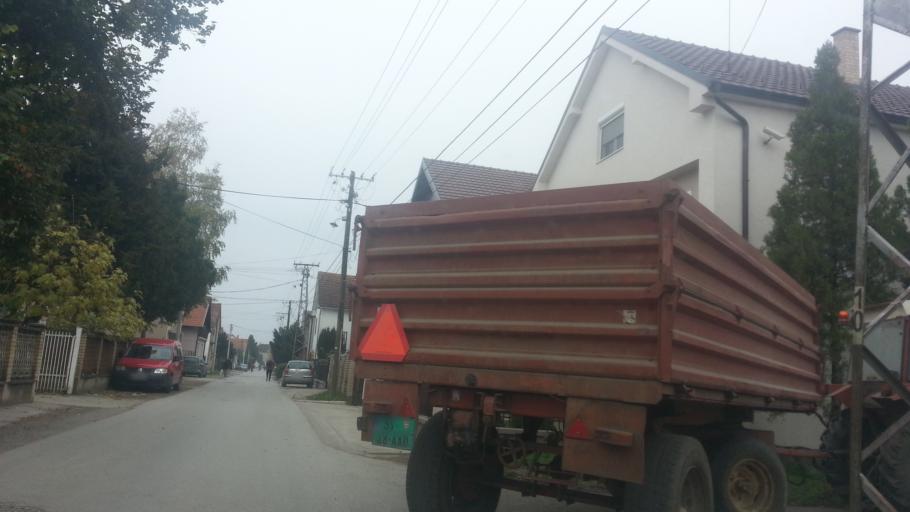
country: RS
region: Autonomna Pokrajina Vojvodina
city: Nova Pazova
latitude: 44.9526
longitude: 20.2129
